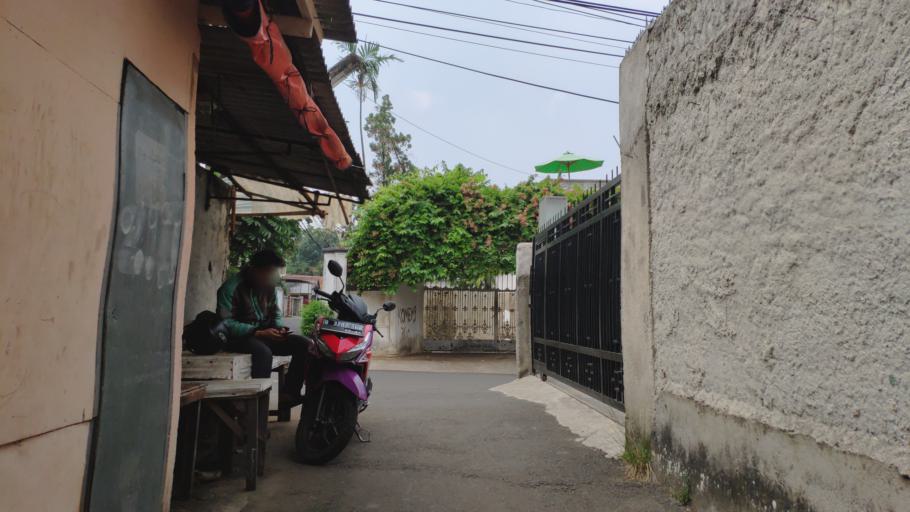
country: ID
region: Banten
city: South Tangerang
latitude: -6.2688
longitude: 106.7716
